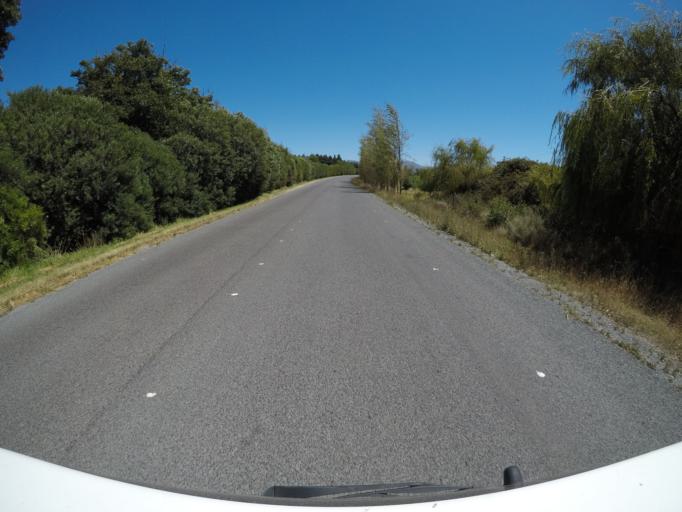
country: ZA
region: Western Cape
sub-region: Overberg District Municipality
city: Grabouw
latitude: -34.1866
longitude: 19.0392
